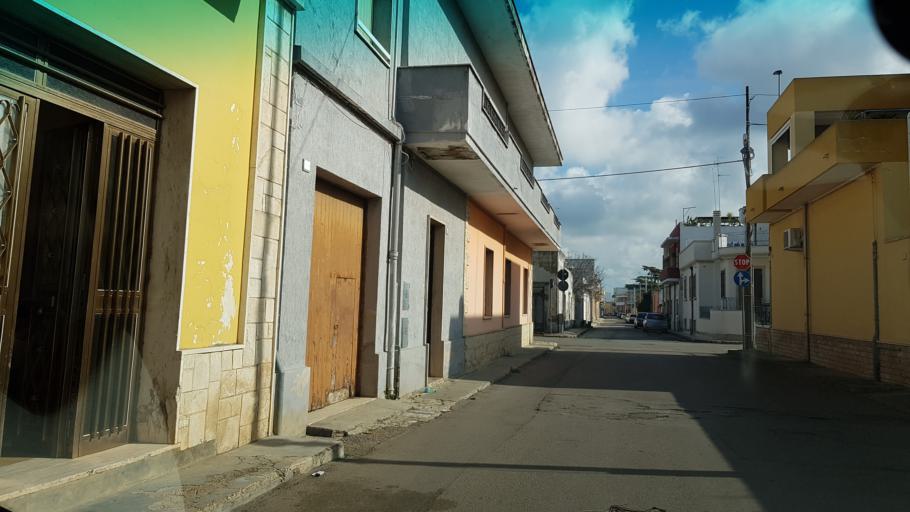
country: IT
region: Apulia
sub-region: Provincia di Brindisi
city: San Pietro Vernotico
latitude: 40.4827
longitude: 17.9981
